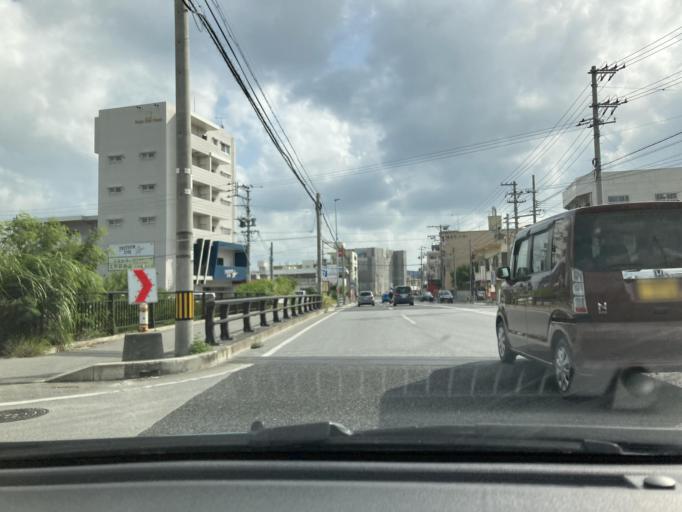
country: JP
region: Okinawa
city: Ginowan
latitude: 26.2218
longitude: 127.7656
